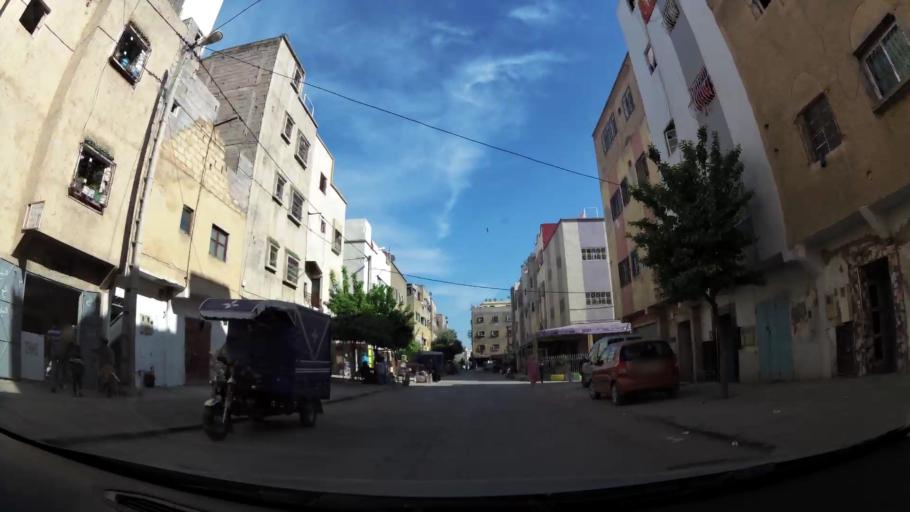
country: MA
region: Fes-Boulemane
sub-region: Fes
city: Fes
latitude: 34.0167
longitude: -5.0329
